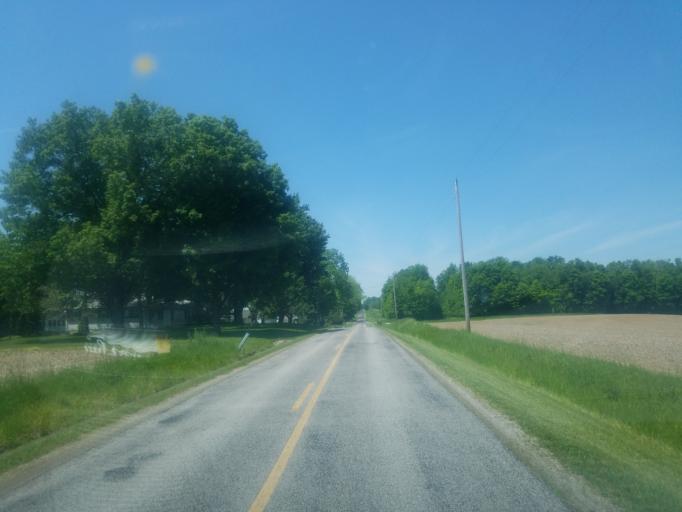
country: US
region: Ohio
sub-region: Huron County
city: New London
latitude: 41.1163
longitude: -82.4164
